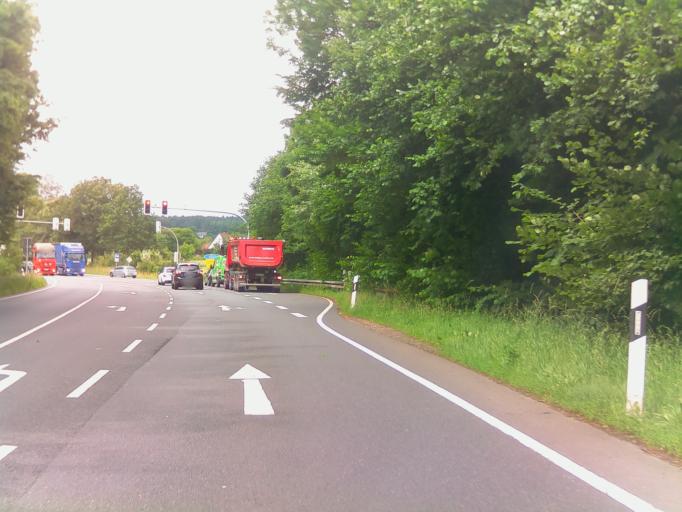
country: DE
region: Lower Saxony
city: Bad Munder am Deister
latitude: 52.1973
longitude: 9.4783
